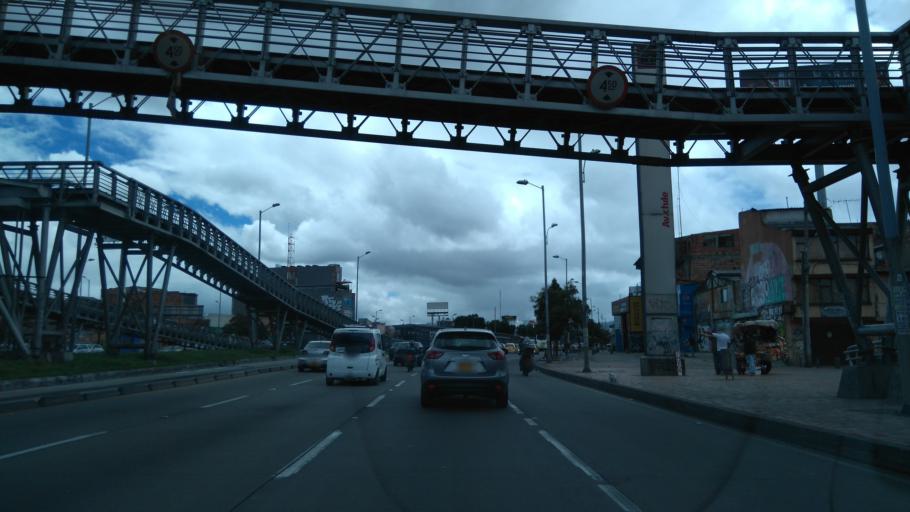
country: CO
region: Bogota D.C.
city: Barrio San Luis
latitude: 4.6647
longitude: -74.0755
